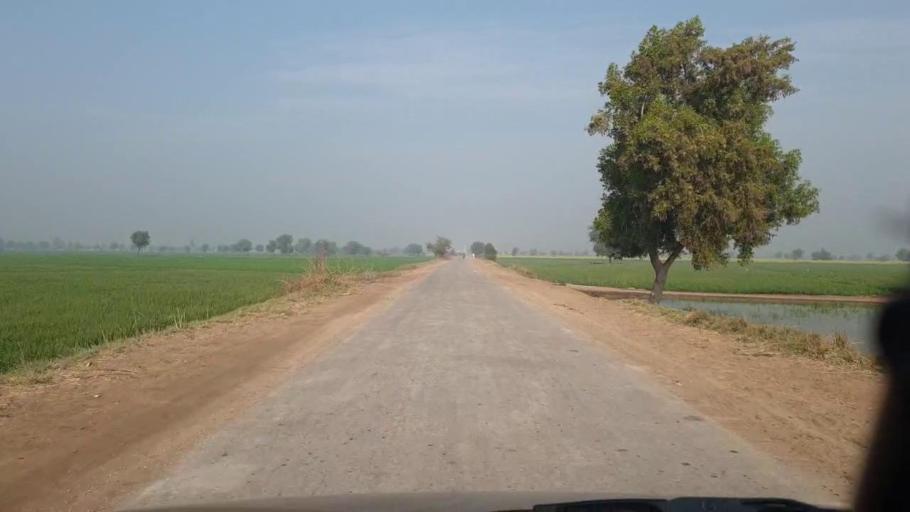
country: PK
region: Sindh
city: Shahdadpur
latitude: 25.9825
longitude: 68.5704
